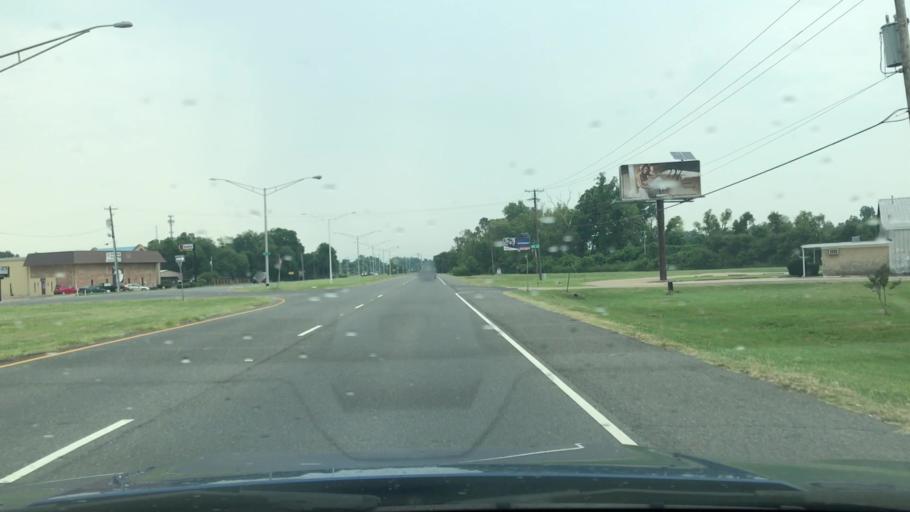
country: US
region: Louisiana
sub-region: Bossier Parish
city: Bossier City
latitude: 32.4059
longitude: -93.6971
